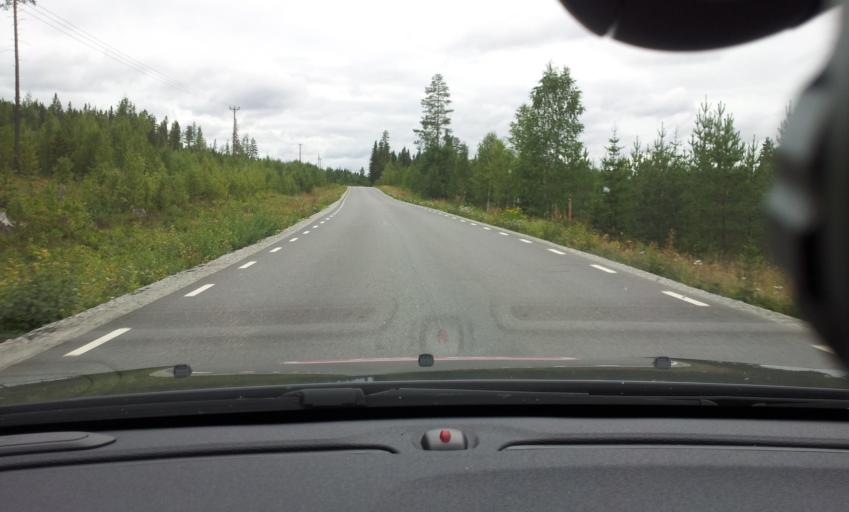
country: SE
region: Jaemtland
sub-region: Braecke Kommun
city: Braecke
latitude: 63.1327
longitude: 15.5093
